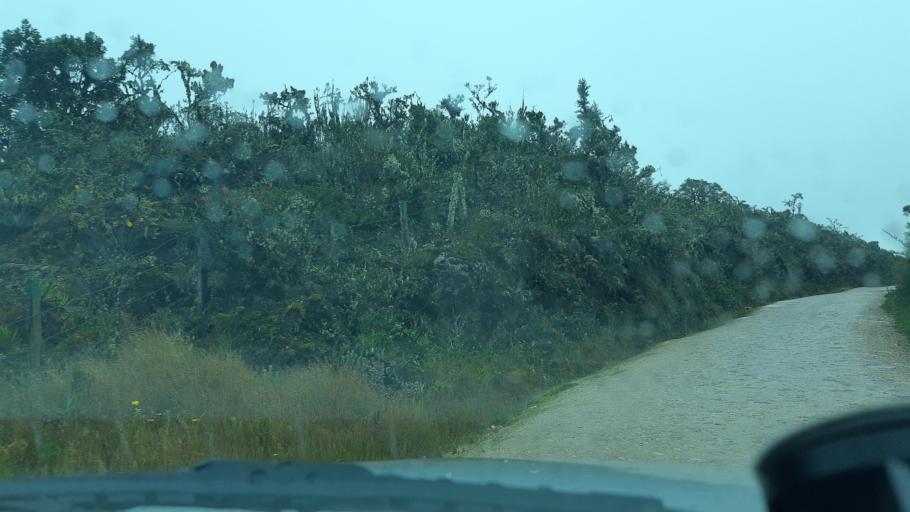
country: CO
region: Cundinamarca
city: Villapinzon
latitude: 5.2168
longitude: -73.5270
